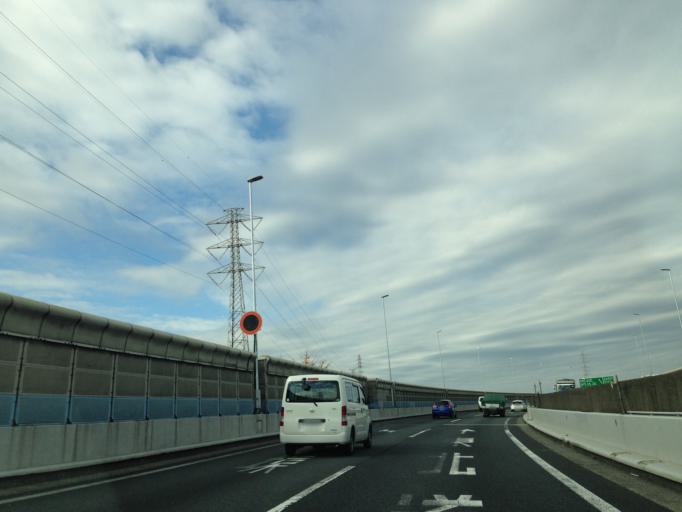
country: JP
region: Saitama
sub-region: Kawaguchi-shi
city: Hatogaya-honcho
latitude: 35.8479
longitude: 139.7365
